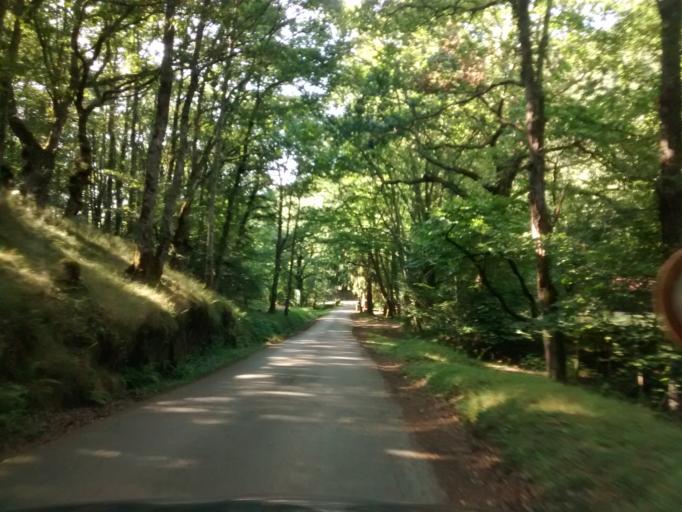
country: ES
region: Cantabria
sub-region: Provincia de Cantabria
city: Ruente
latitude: 43.2378
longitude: -4.2263
